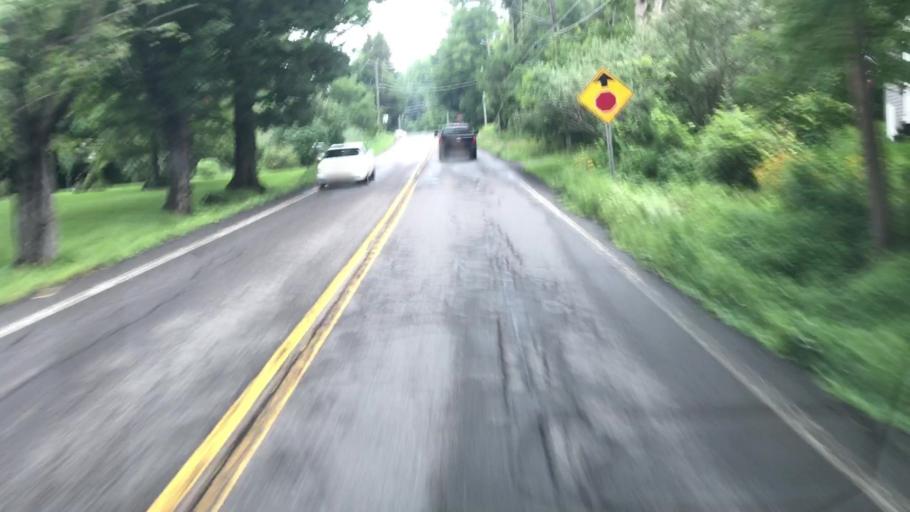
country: US
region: New York
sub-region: Onondaga County
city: Skaneateles
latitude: 42.9623
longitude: -76.4375
